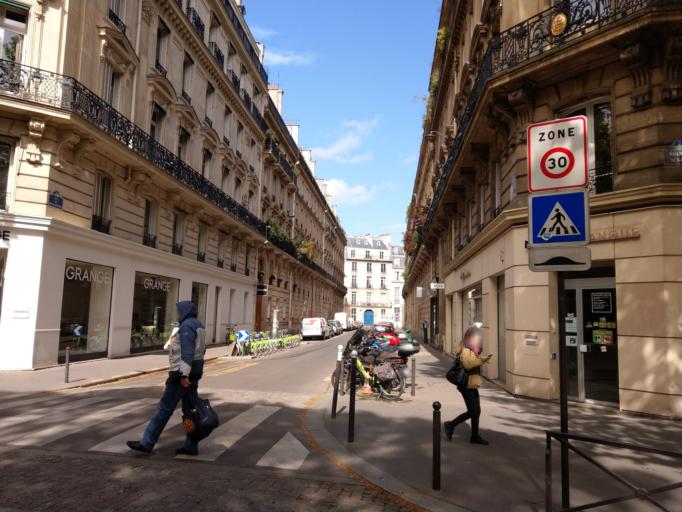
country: FR
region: Ile-de-France
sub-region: Paris
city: Paris
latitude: 48.8581
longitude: 2.3236
